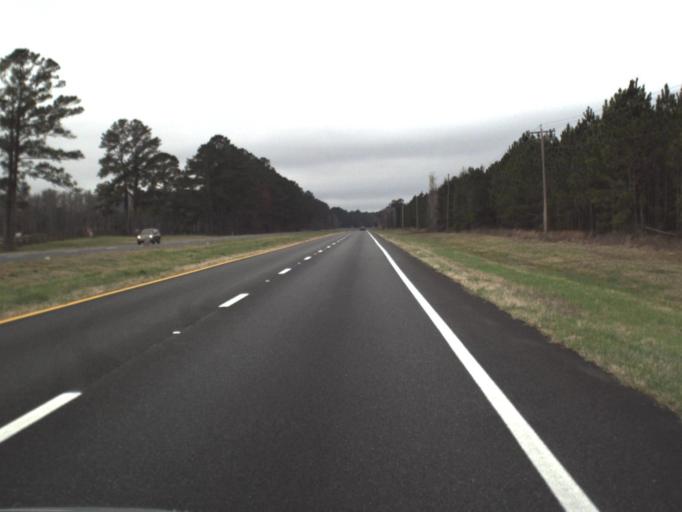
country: US
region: Florida
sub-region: Jefferson County
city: Monticello
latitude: 30.3878
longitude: -83.8456
